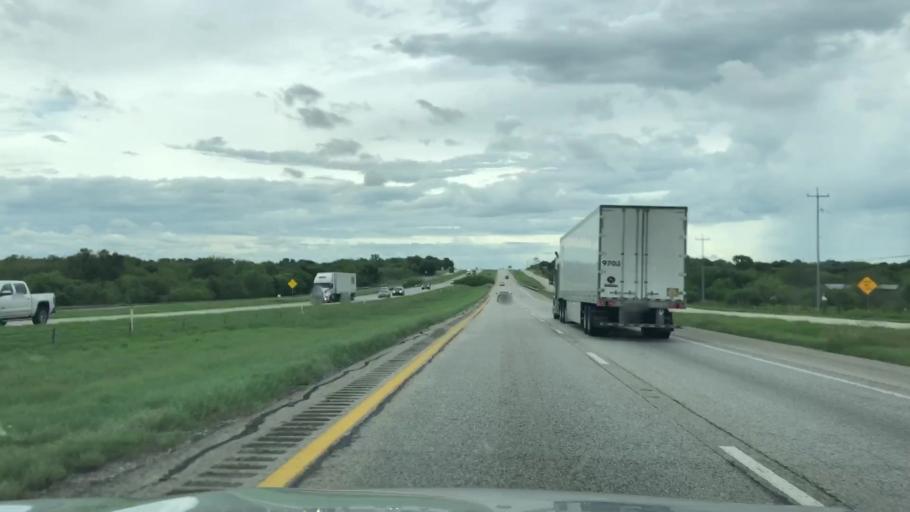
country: US
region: Texas
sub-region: Guadalupe County
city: Cibolo
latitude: 29.4920
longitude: -98.2112
